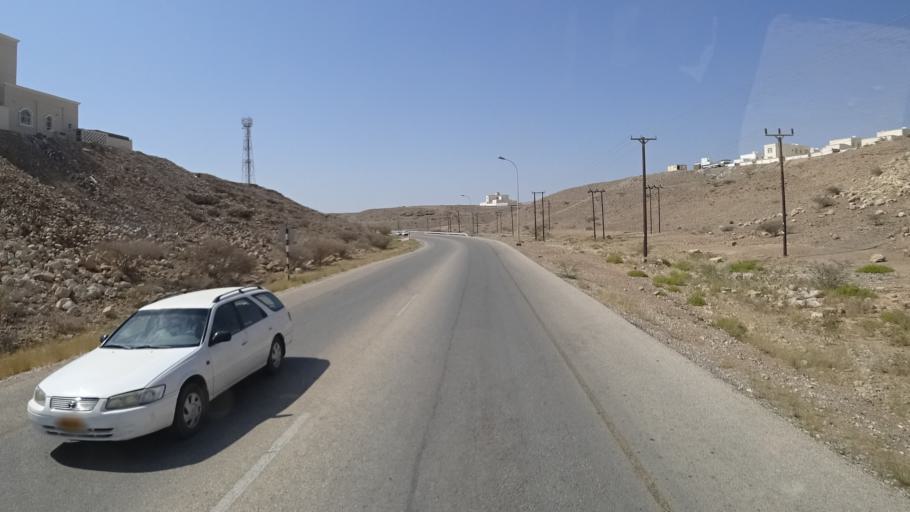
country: OM
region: Ash Sharqiyah
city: Sur
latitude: 22.5511
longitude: 59.4985
